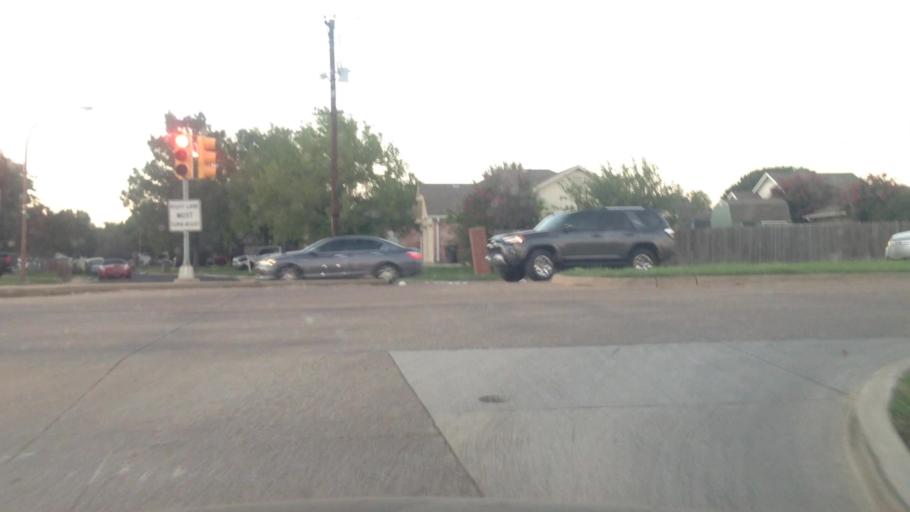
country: US
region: Texas
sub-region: Tarrant County
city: Watauga
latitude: 32.8608
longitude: -97.2805
